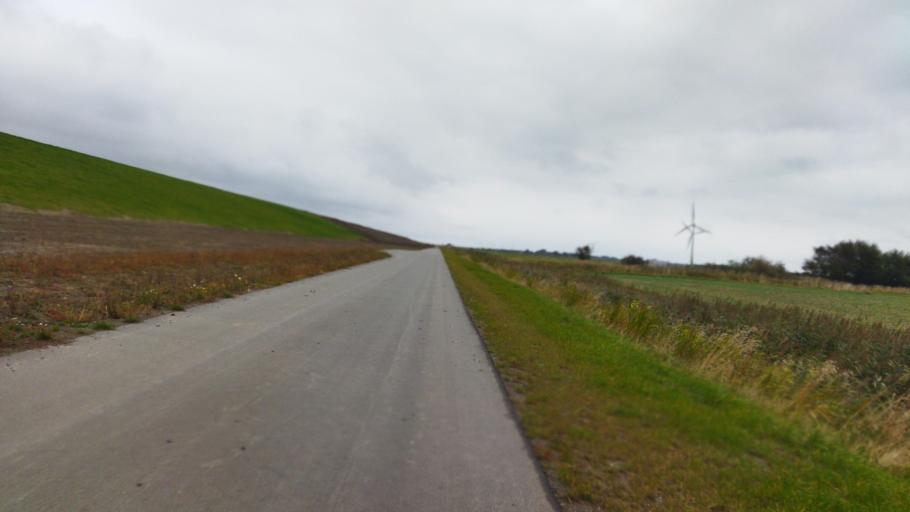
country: NL
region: Groningen
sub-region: Gemeente Delfzijl
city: Delfzijl
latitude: 53.4378
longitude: 7.0186
